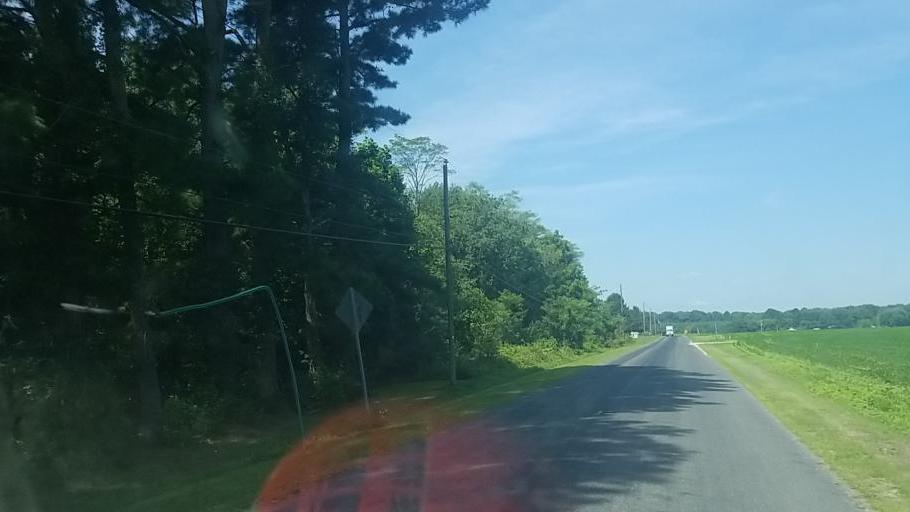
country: US
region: Maryland
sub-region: Caroline County
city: Denton
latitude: 38.8781
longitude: -75.7899
